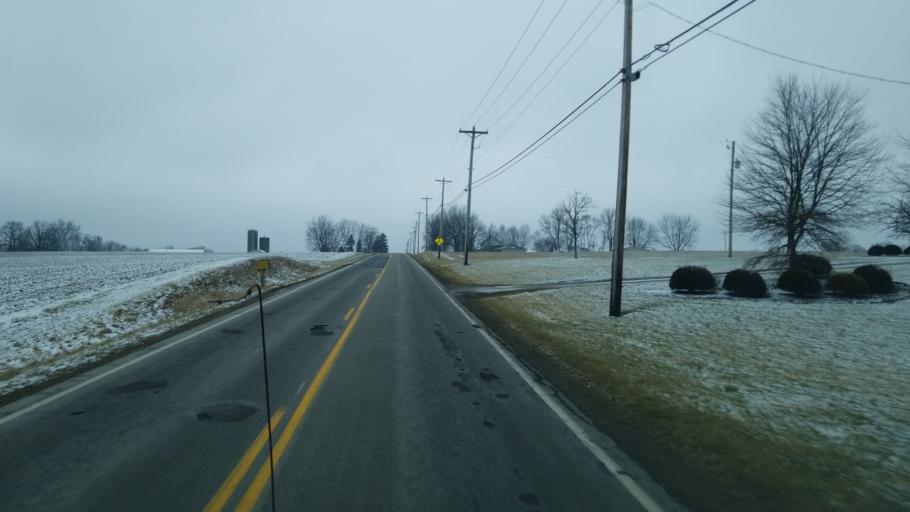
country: US
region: Ohio
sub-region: Wayne County
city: Apple Creek
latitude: 40.7899
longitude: -81.8440
